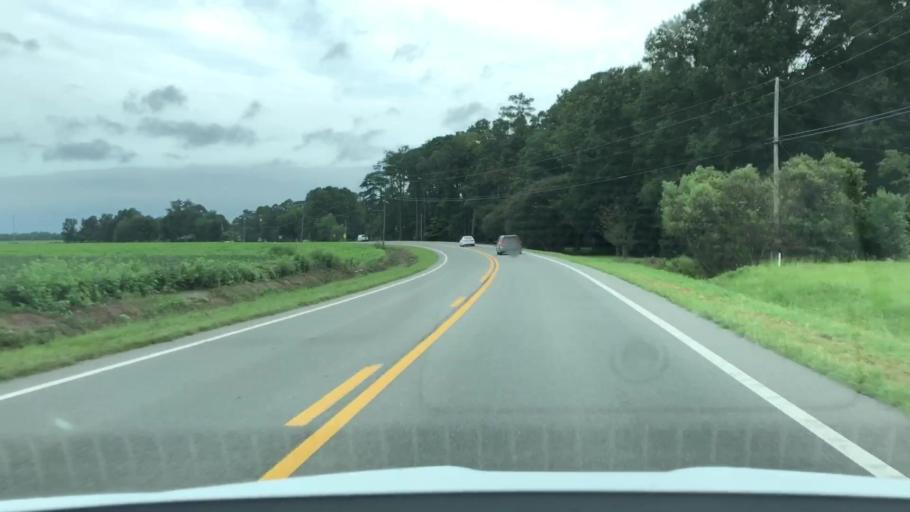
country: US
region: North Carolina
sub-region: Lenoir County
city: Kinston
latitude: 35.2029
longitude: -77.5618
